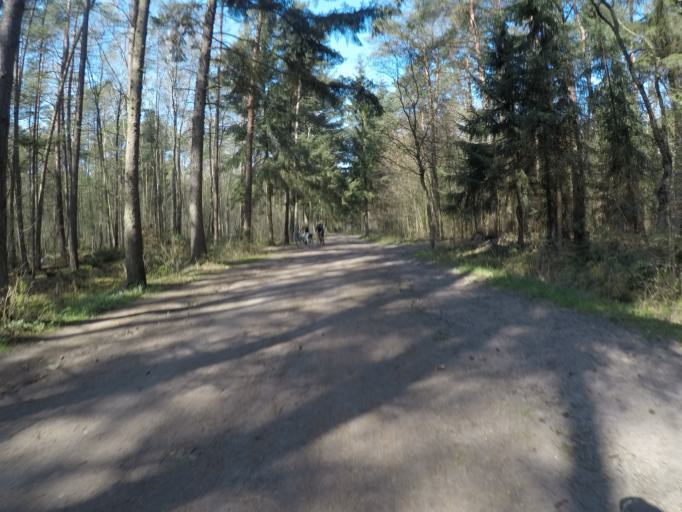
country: DE
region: Schleswig-Holstein
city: Appen
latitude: 53.6203
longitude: 9.7718
